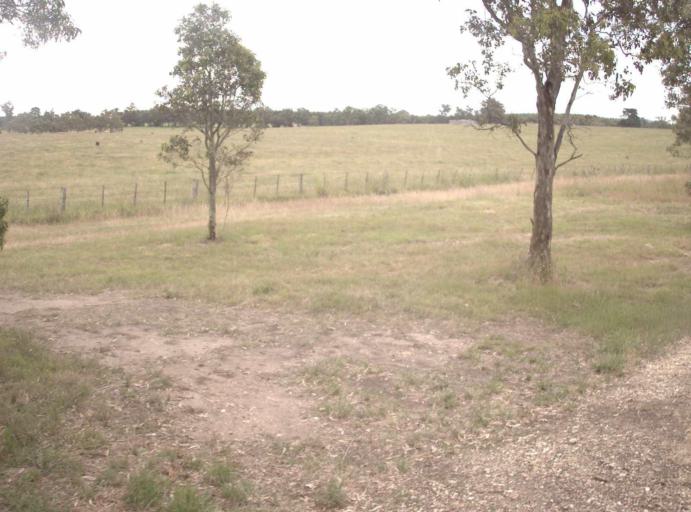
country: AU
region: Victoria
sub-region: East Gippsland
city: Bairnsdale
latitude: -37.7981
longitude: 147.3378
